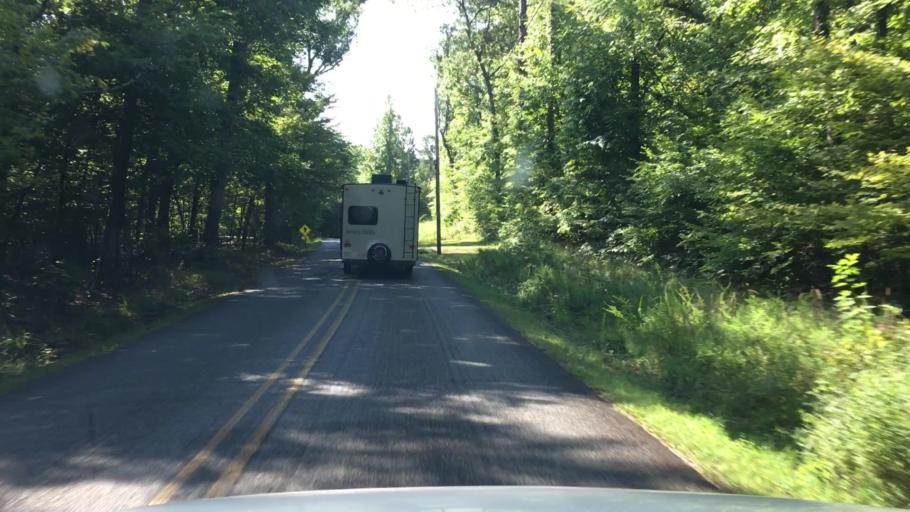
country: US
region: Arkansas
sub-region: Garland County
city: Piney
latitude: 34.5364
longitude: -93.3407
